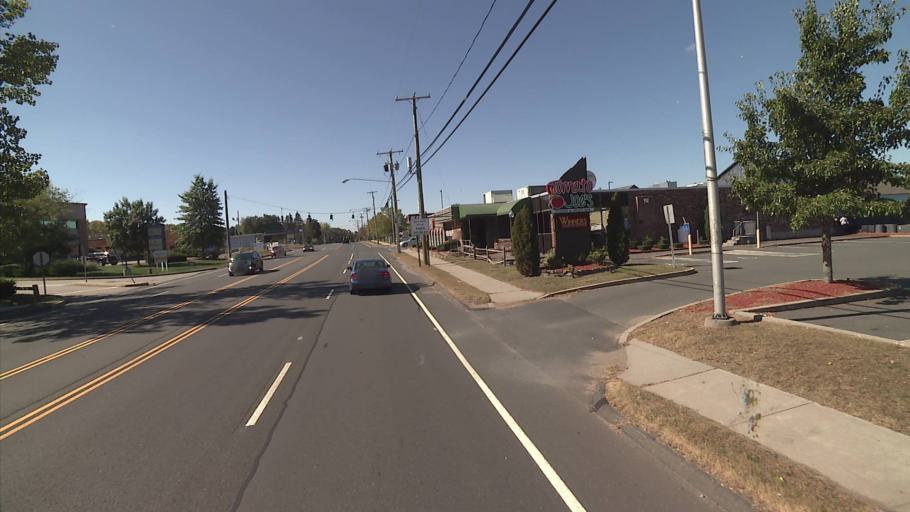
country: US
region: Connecticut
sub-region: Hartford County
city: Manchester
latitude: 41.8138
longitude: -72.5099
